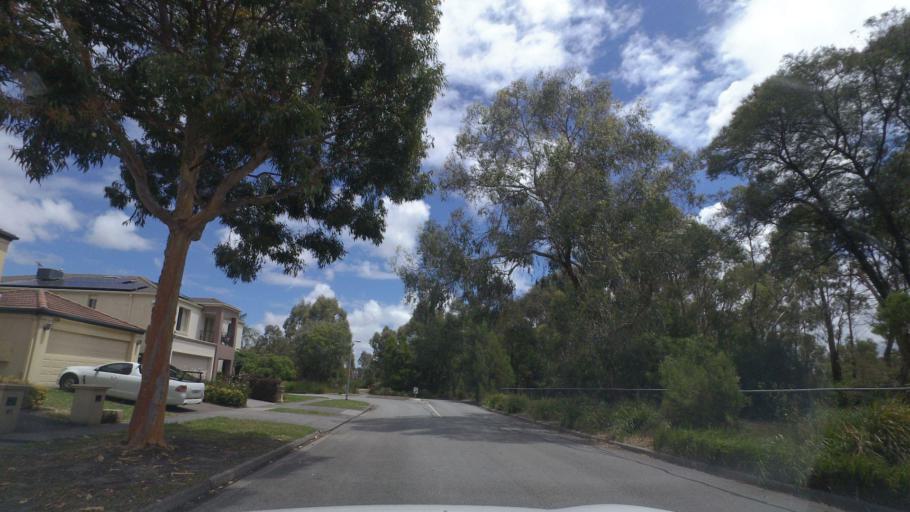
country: AU
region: Victoria
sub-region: Knox
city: Knoxfield
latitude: -37.9009
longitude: 145.2703
